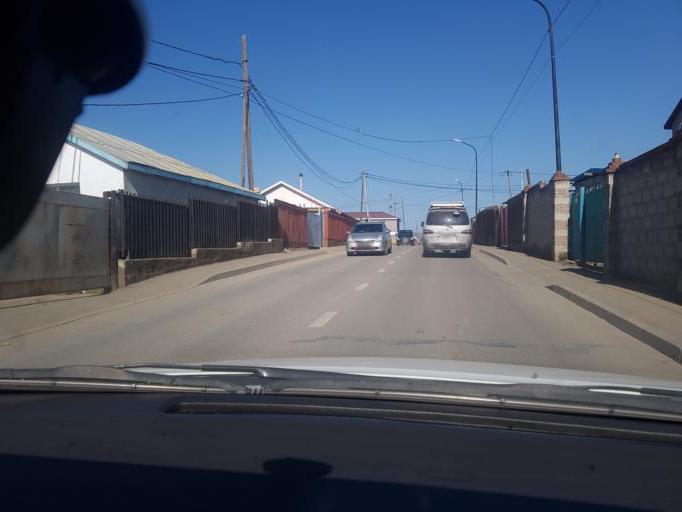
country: MN
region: Ulaanbaatar
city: Ulaanbaatar
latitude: 47.9505
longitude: 106.8623
